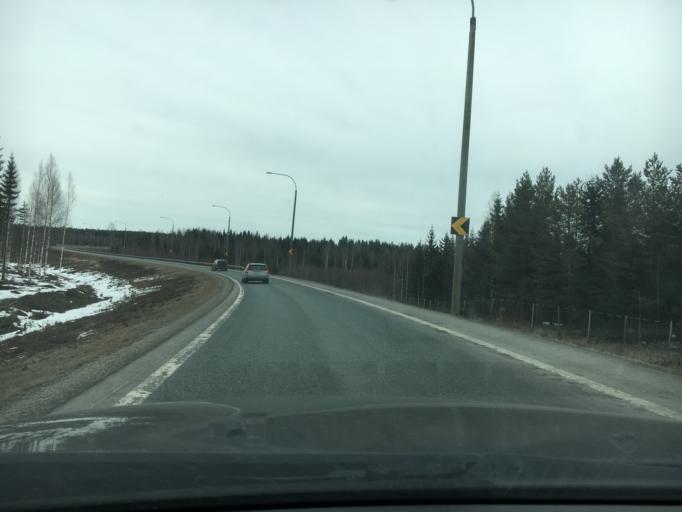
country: FI
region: Northern Savo
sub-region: Kuopio
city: Kuopio
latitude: 62.7179
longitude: 27.5813
